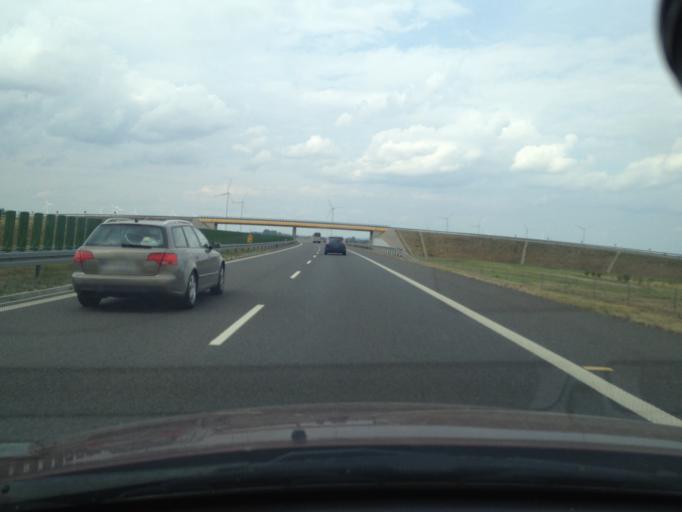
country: PL
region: West Pomeranian Voivodeship
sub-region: Powiat pyrzycki
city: Kozielice
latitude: 53.0781
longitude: 14.8562
